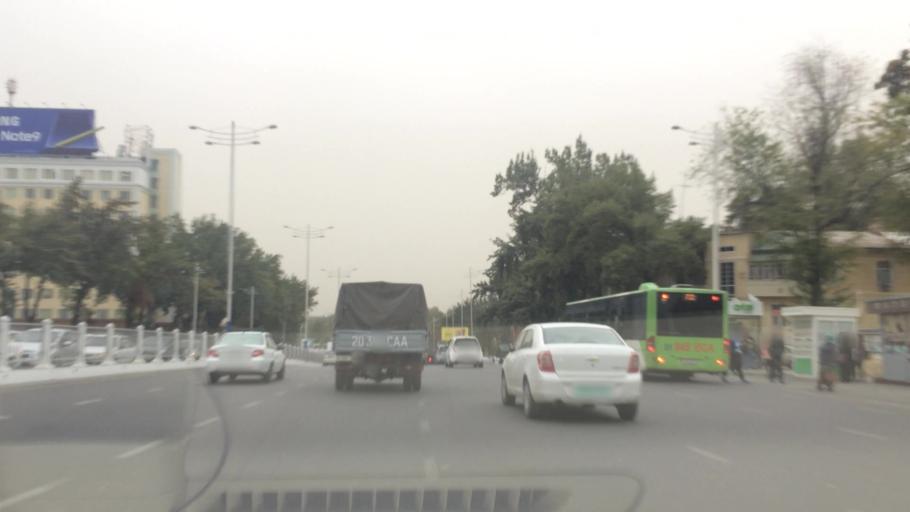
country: UZ
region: Toshkent Shahri
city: Tashkent
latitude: 41.3057
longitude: 69.3064
